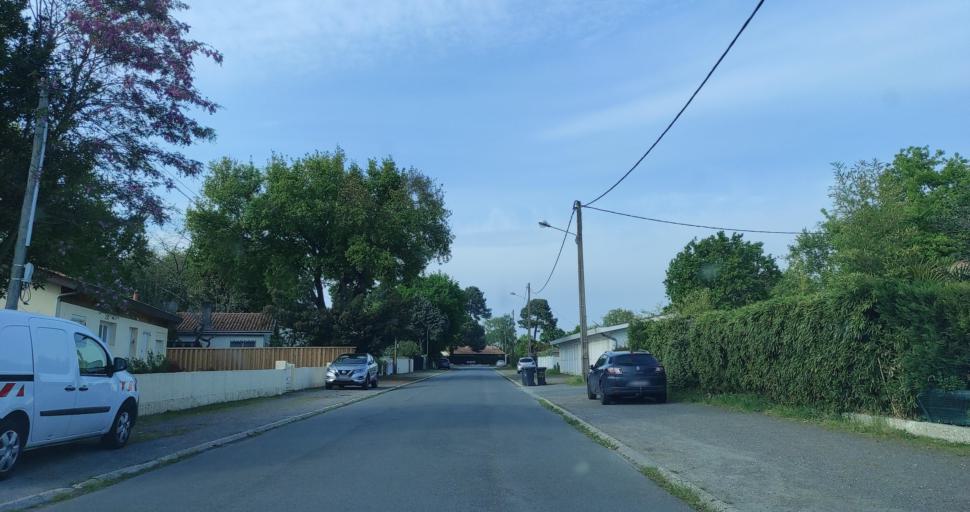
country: FR
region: Aquitaine
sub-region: Departement de la Gironde
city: Ares
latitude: 44.7627
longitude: -1.1285
